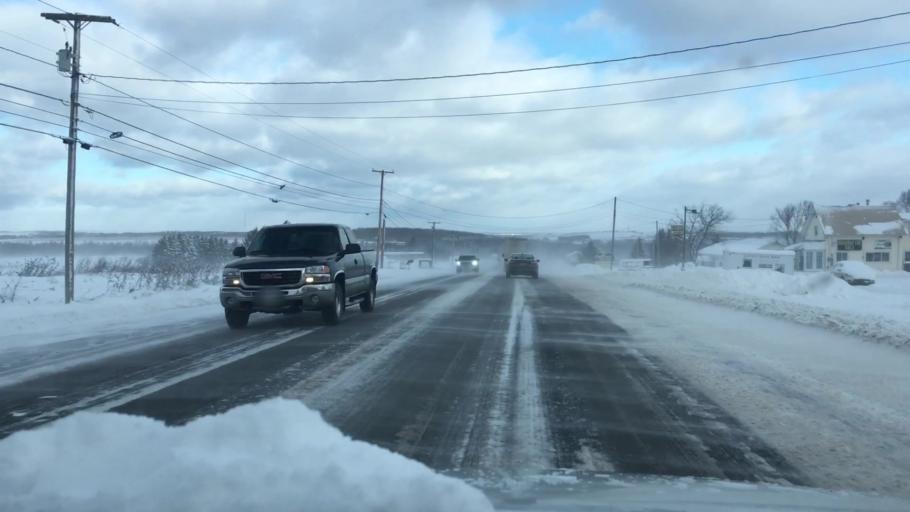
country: US
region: Maine
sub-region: Aroostook County
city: Caribou
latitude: 46.7940
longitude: -67.9913
